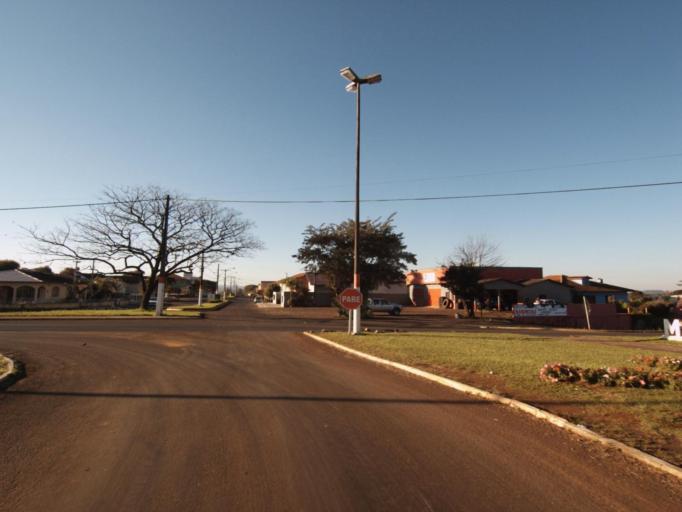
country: BR
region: Santa Catarina
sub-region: Chapeco
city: Chapeco
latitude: -26.9053
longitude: -52.9032
